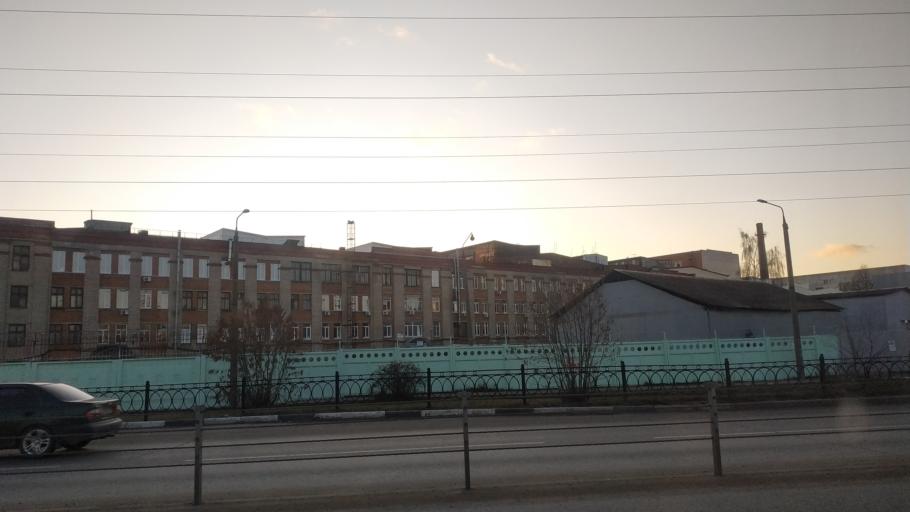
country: RU
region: Moskovskaya
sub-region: Podol'skiy Rayon
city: Podol'sk
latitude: 55.4149
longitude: 37.5786
